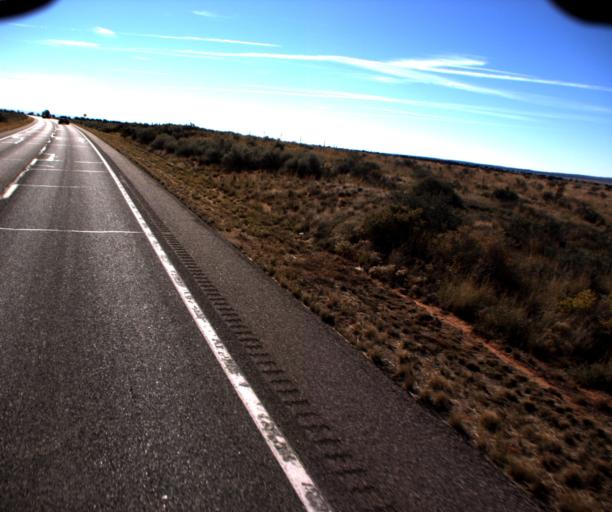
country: US
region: Arizona
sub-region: Mohave County
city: Colorado City
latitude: 36.8861
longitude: -112.9056
